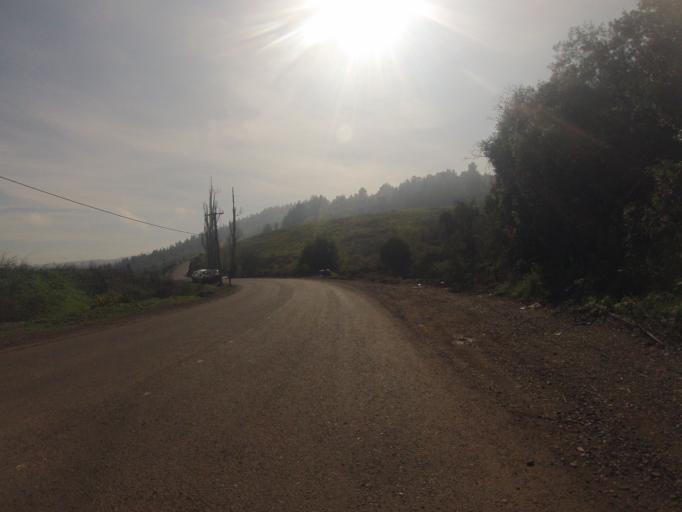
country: CL
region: Araucania
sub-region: Provincia de Cautin
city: Temuco
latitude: -38.7225
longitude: -72.6006
